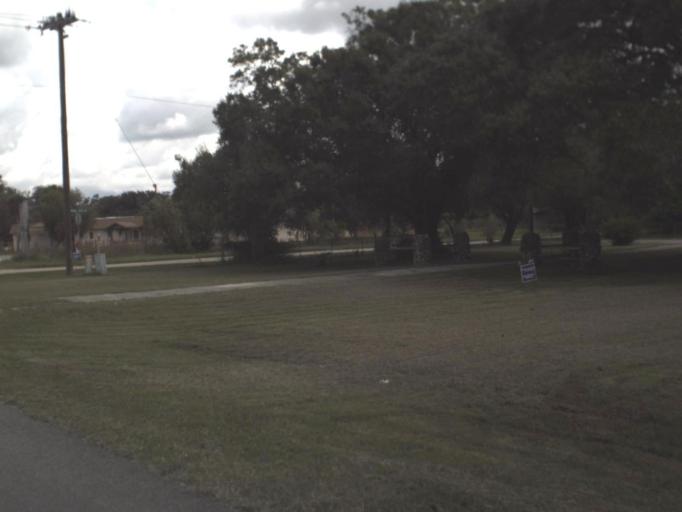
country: US
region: Florida
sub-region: Hendry County
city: LaBelle
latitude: 26.7831
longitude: -81.4372
